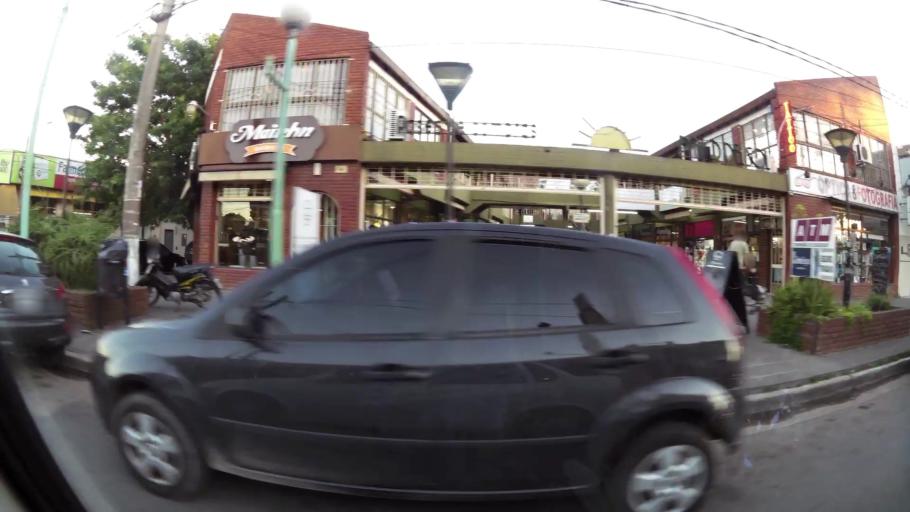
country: AR
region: Buenos Aires
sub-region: Partido de Quilmes
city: Quilmes
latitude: -34.8086
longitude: -58.1866
